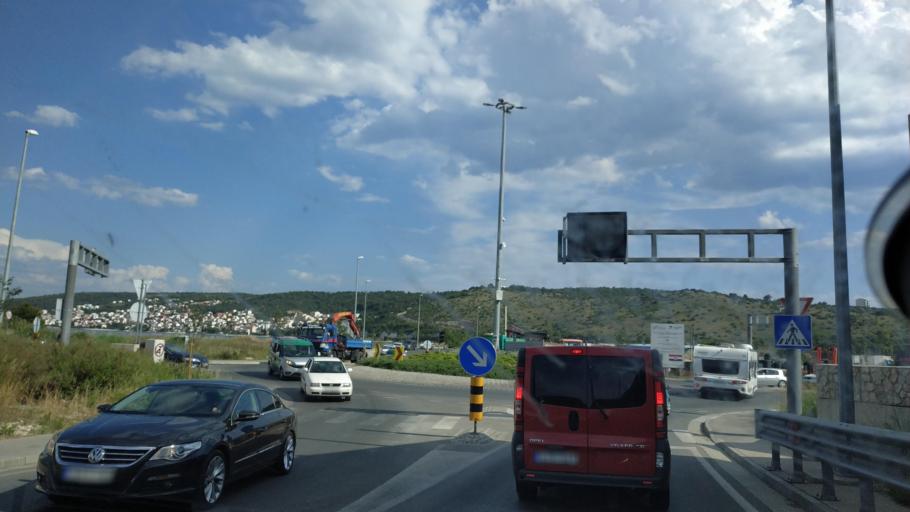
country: HR
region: Splitsko-Dalmatinska
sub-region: Grad Trogir
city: Trogir
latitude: 43.5231
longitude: 16.2640
